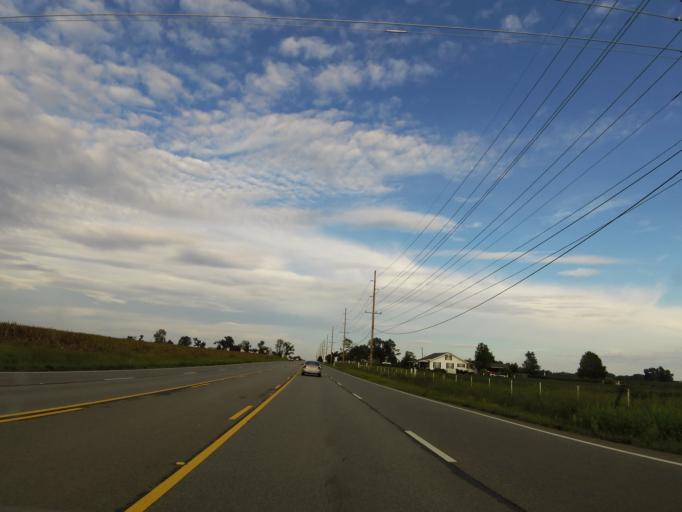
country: US
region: Alabama
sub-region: Limestone County
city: Athens
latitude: 34.7955
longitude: -87.1233
